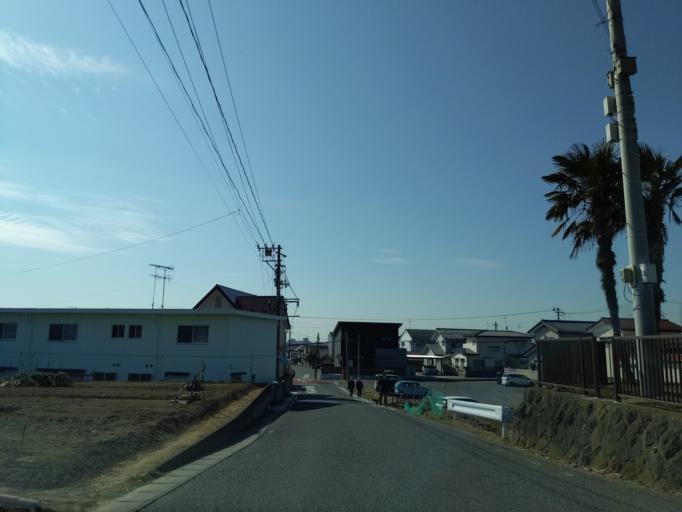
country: JP
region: Fukushima
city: Koriyama
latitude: 37.4254
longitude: 140.3530
